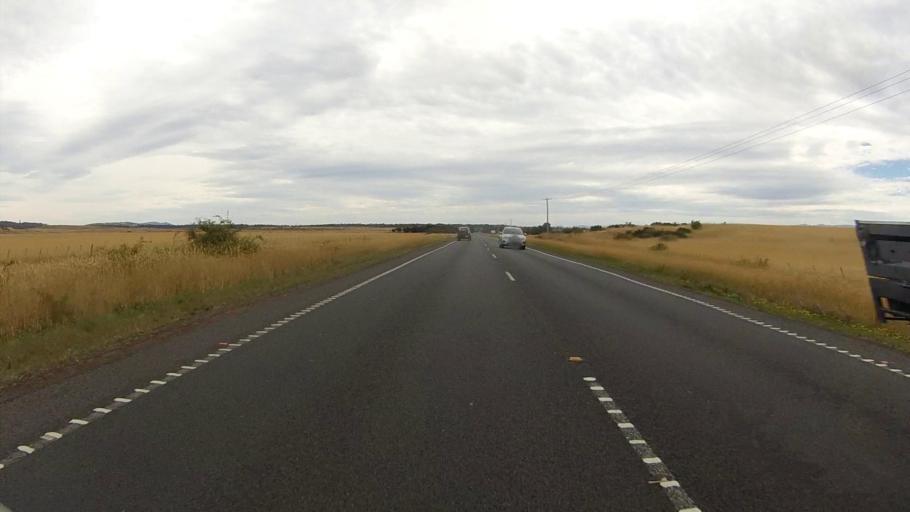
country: AU
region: Tasmania
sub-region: Northern Midlands
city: Evandale
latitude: -41.8603
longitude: 147.4555
